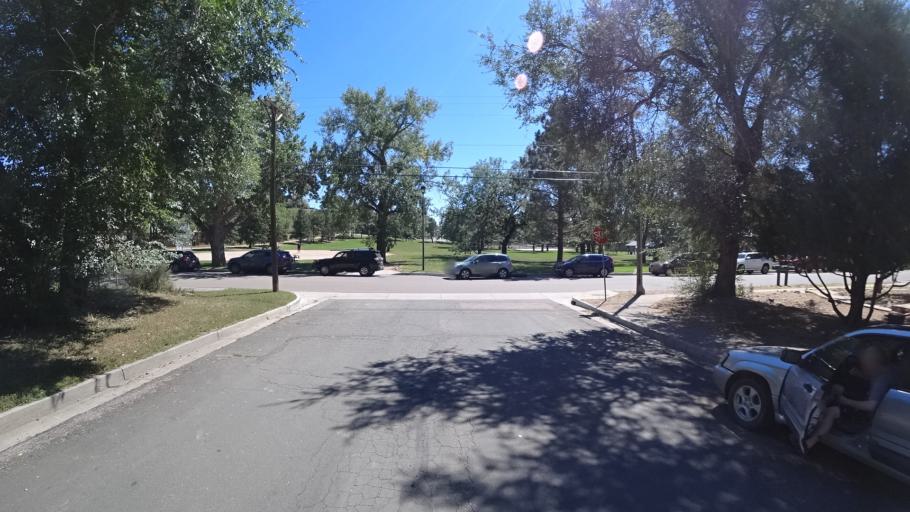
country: US
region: Colorado
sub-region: El Paso County
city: Colorado Springs
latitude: 38.8505
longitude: -104.8572
